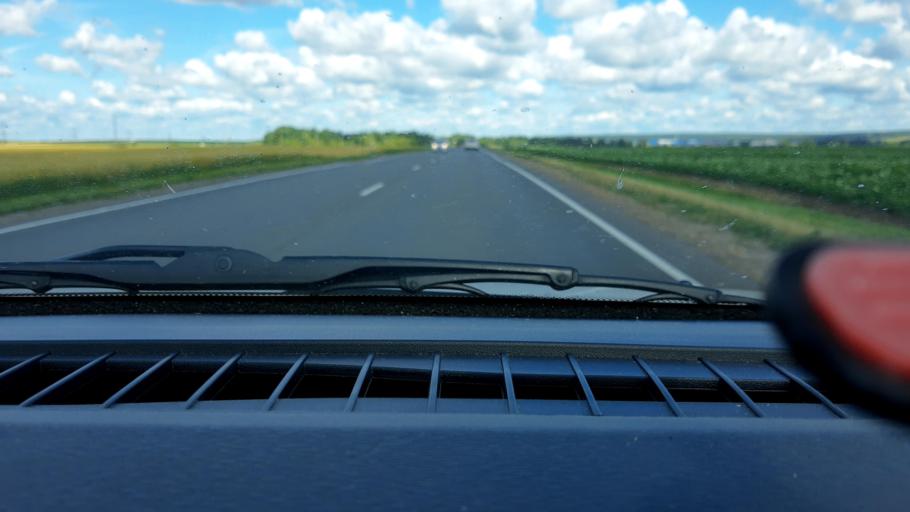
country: RU
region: Nizjnij Novgorod
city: Arzamas
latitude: 55.2767
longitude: 43.9592
